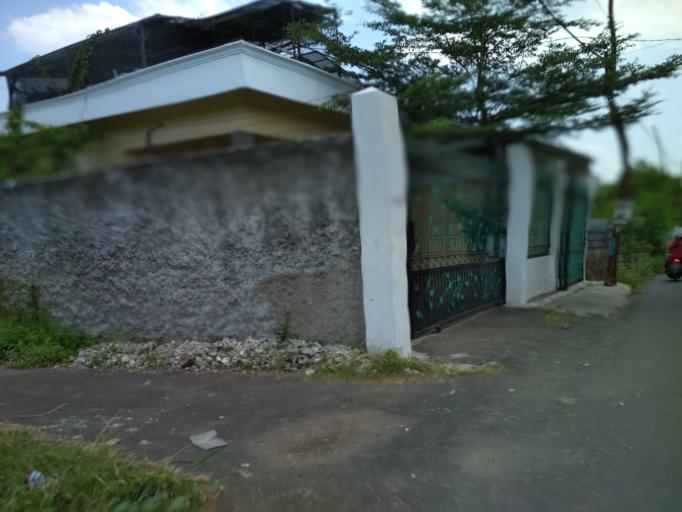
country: ID
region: West Java
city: Ciampea
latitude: -6.5626
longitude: 106.7440
